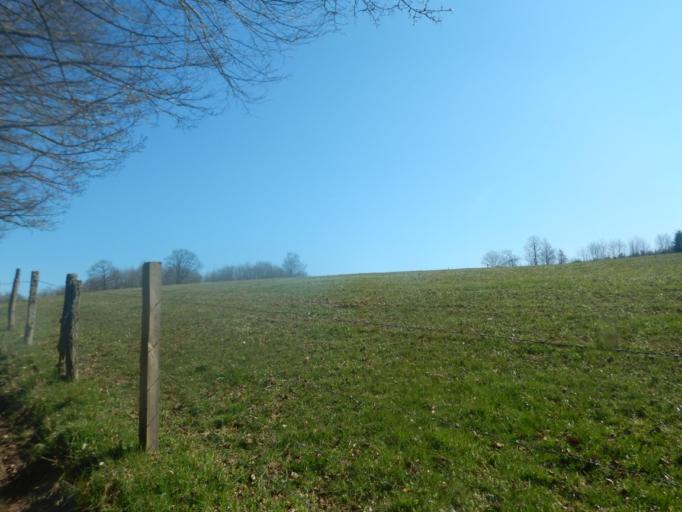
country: LU
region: Diekirch
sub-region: Canton de Wiltz
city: Wiltz
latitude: 49.9555
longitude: 5.9535
